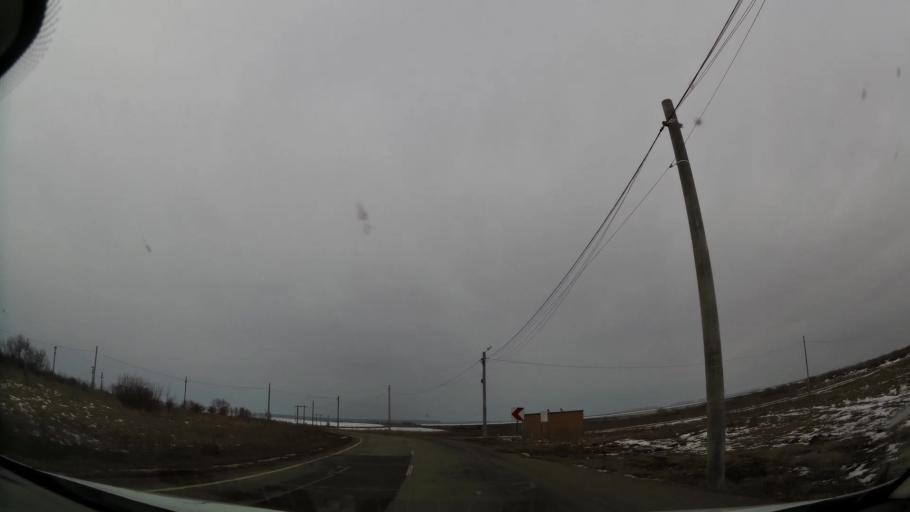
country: RO
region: Ilfov
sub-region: Comuna Tunari
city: Tunari
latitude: 44.5459
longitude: 26.1610
